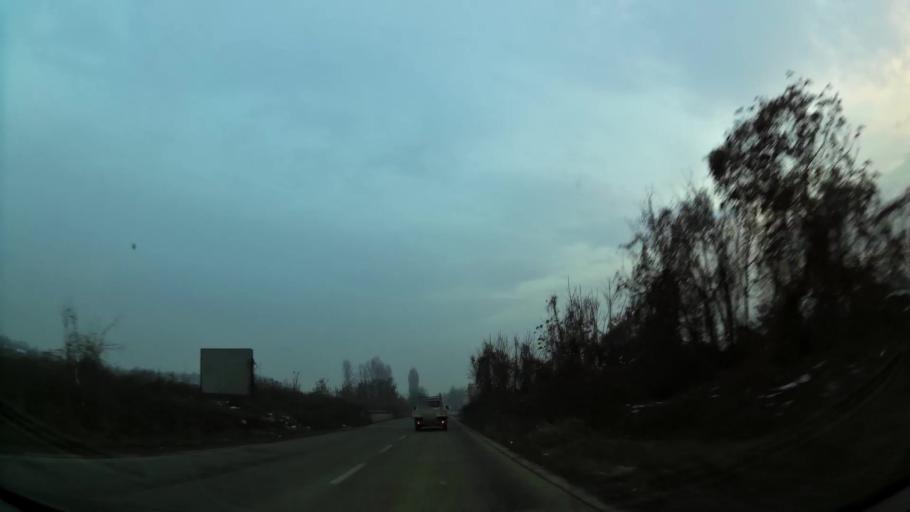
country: MK
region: Suto Orizari
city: Suto Orizare
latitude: 42.0199
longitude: 21.4101
